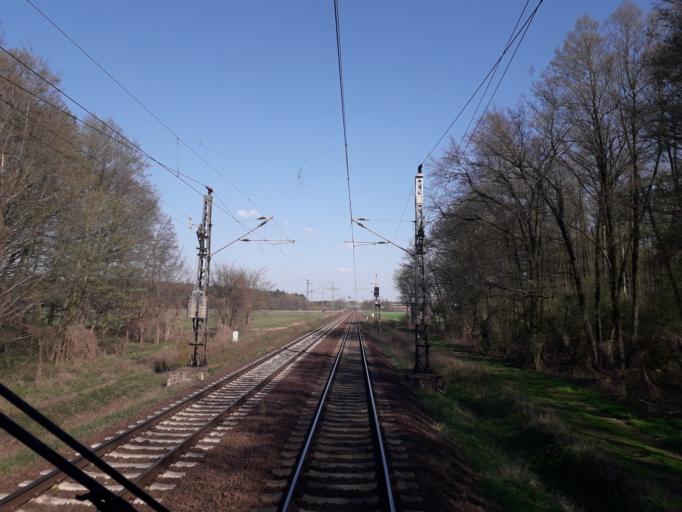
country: DE
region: Brandenburg
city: Stahnsdorf
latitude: 52.3201
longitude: 13.1808
